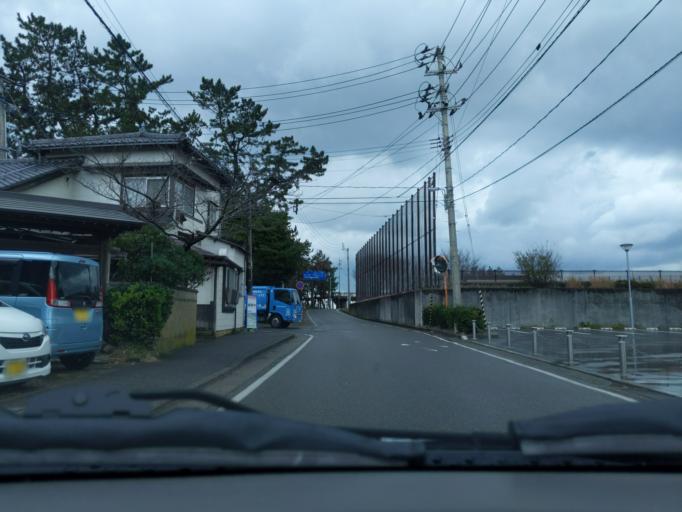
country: JP
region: Niigata
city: Niigata-shi
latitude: 37.9287
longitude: 139.0381
